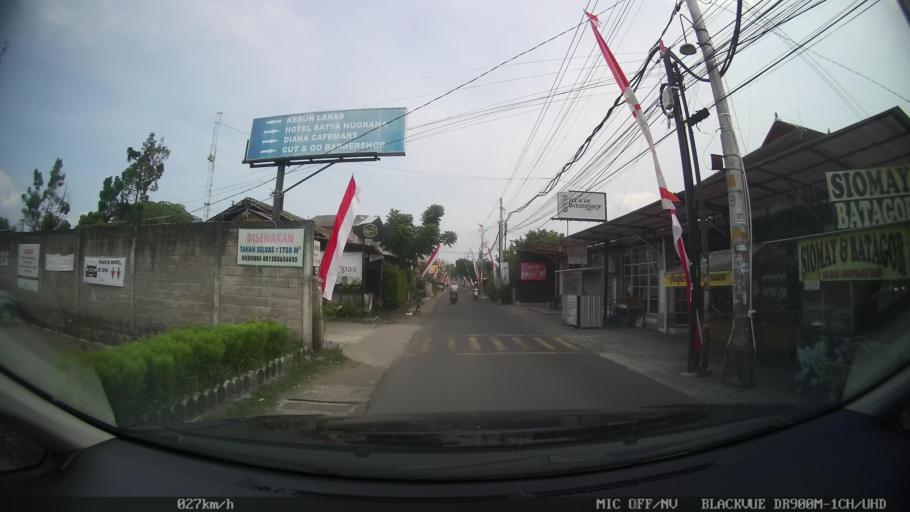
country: ID
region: Daerah Istimewa Yogyakarta
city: Yogyakarta
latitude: -7.7895
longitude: 110.3985
